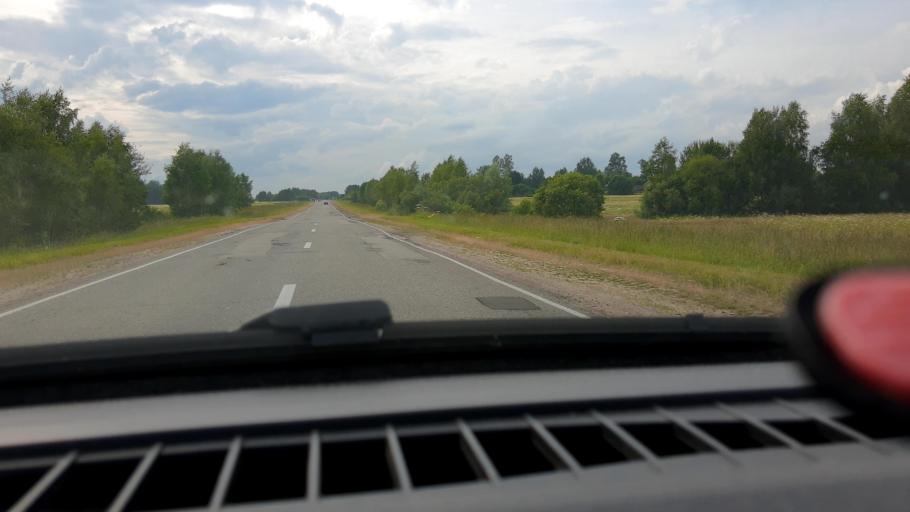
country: RU
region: Nizjnij Novgorod
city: Neklyudovo
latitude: 56.5026
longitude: 43.9847
